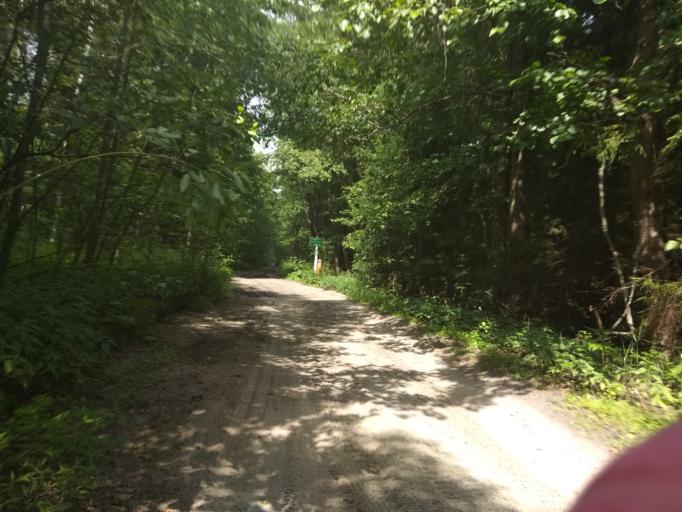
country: RU
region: Moskovskaya
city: Misheronskiy
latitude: 55.7291
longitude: 39.7604
